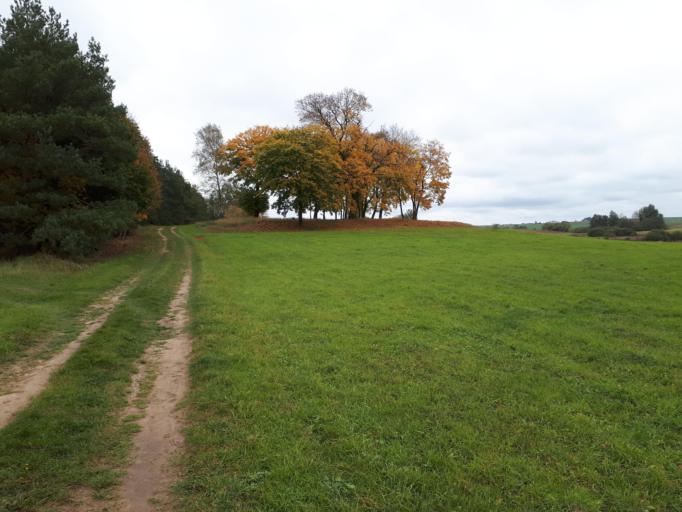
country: LT
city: Kalvarija
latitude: 54.4325
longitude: 23.3406
